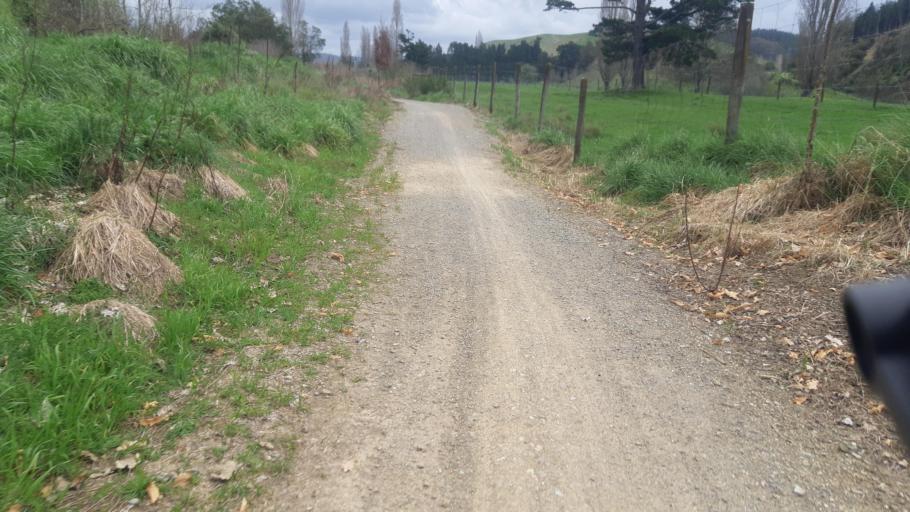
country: NZ
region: Tasman
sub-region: Tasman District
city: Wakefield
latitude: -41.4103
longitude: 173.0109
